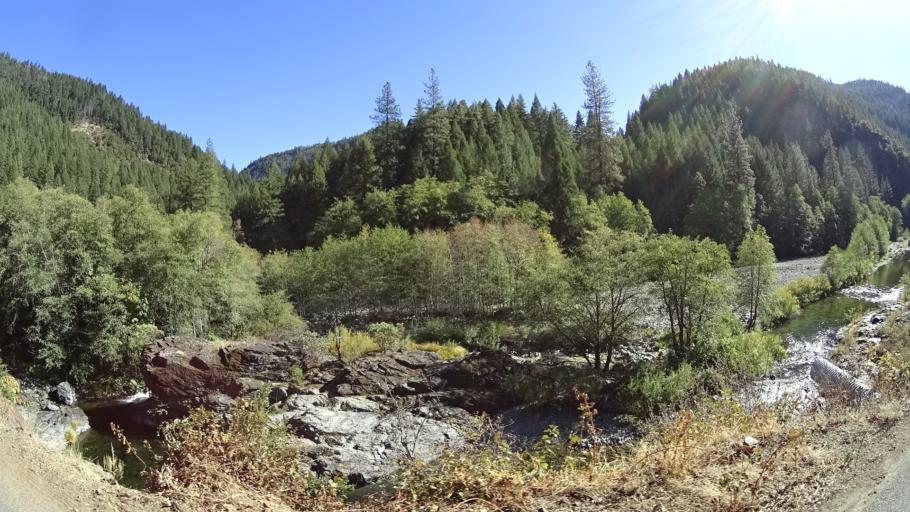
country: US
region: California
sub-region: Siskiyou County
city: Happy Camp
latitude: 41.3000
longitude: -123.1237
